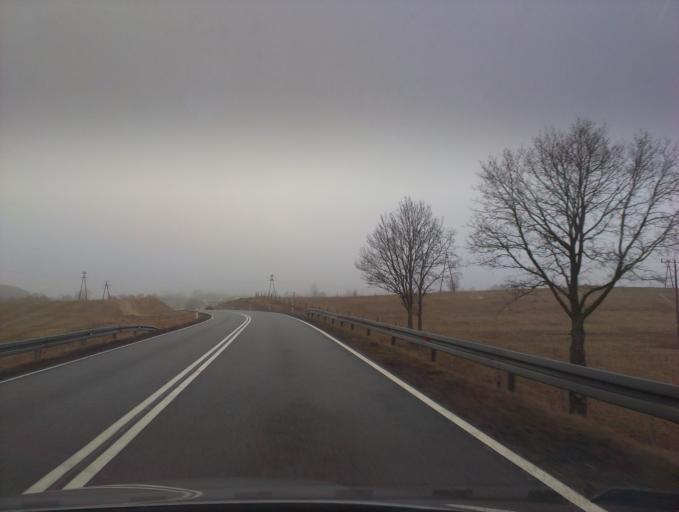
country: PL
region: West Pomeranian Voivodeship
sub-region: Powiat koszalinski
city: Bobolice
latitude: 53.8523
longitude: 16.6158
